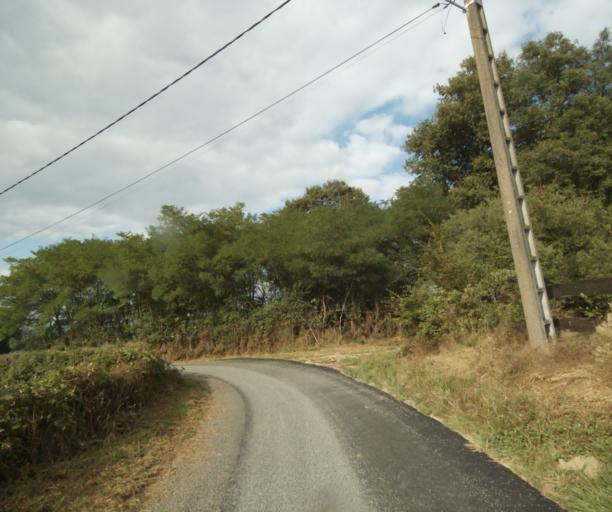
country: FR
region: Bourgogne
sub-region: Departement de Saone-et-Loire
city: Palinges
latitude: 46.5246
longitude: 4.2918
